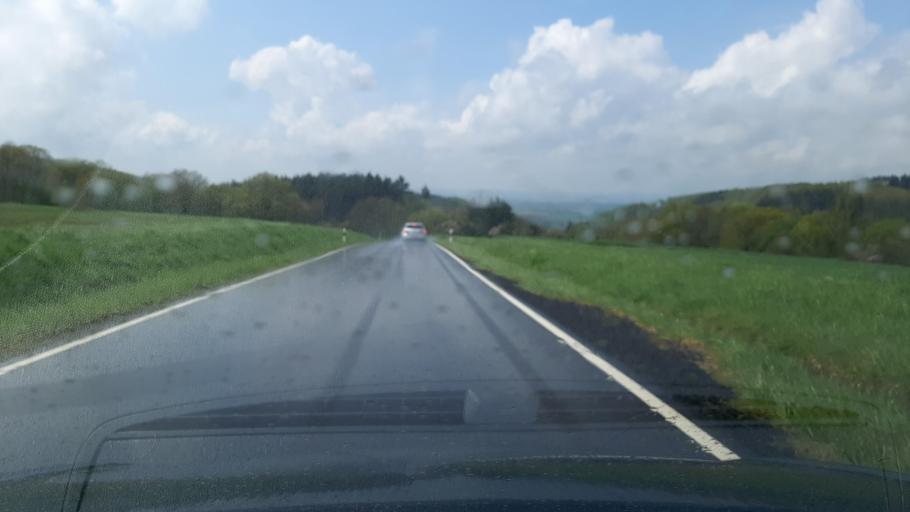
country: DE
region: Rheinland-Pfalz
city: Alken
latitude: 50.2504
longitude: 7.4803
